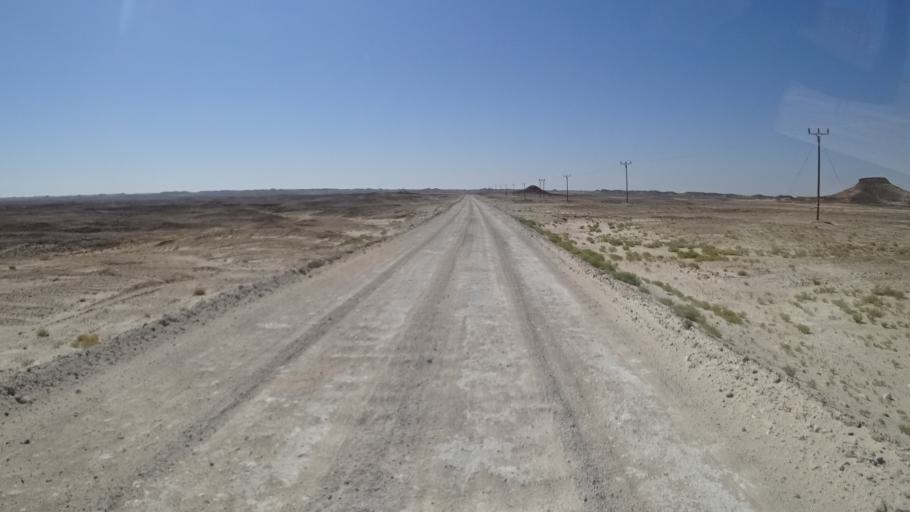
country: YE
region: Al Mahrah
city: Hawf
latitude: 17.3772
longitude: 53.2124
